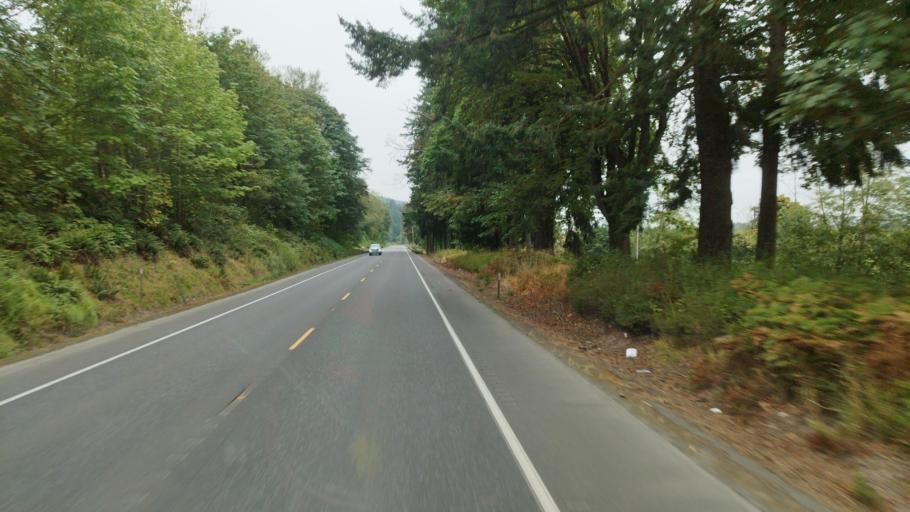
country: US
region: Washington
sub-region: Cowlitz County
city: Kalama
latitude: 45.9540
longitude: -122.8645
